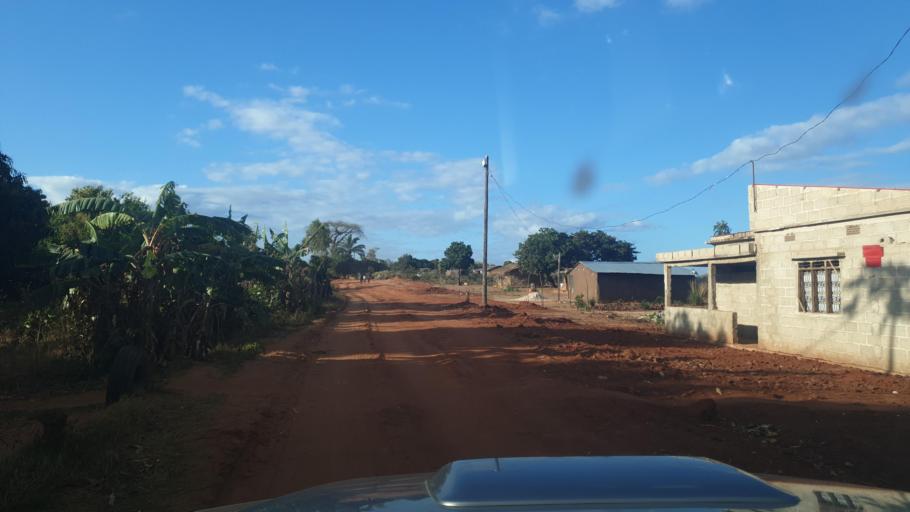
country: MZ
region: Nampula
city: Nampula
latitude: -15.1553
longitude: 39.2648
